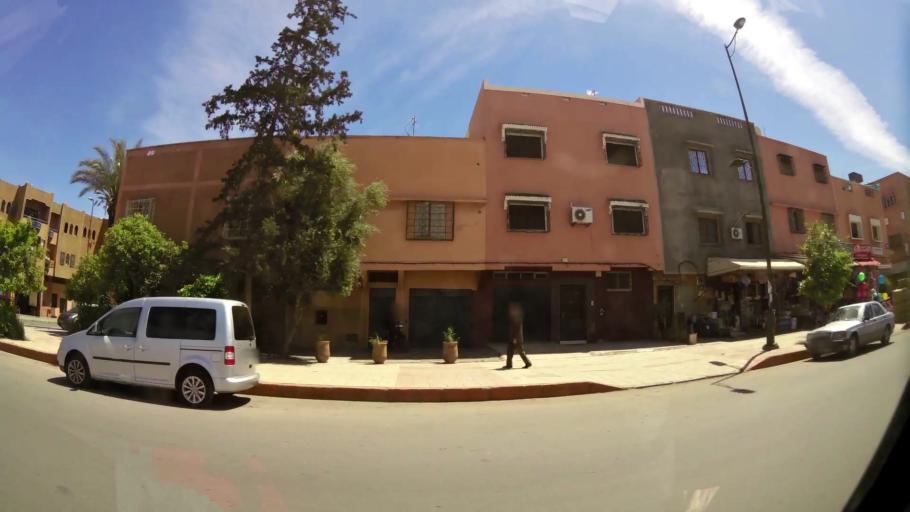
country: MA
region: Marrakech-Tensift-Al Haouz
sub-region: Marrakech
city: Marrakesh
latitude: 31.6502
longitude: -7.9964
